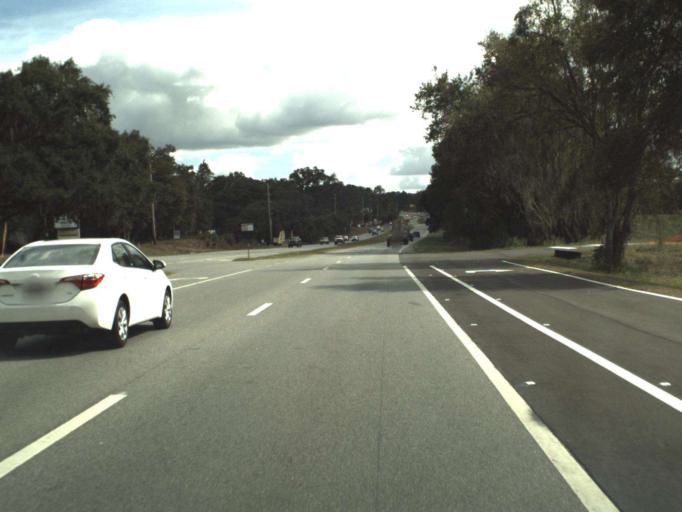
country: US
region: Florida
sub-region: Leon County
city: Tallahassee
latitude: 30.5190
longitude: -84.3491
